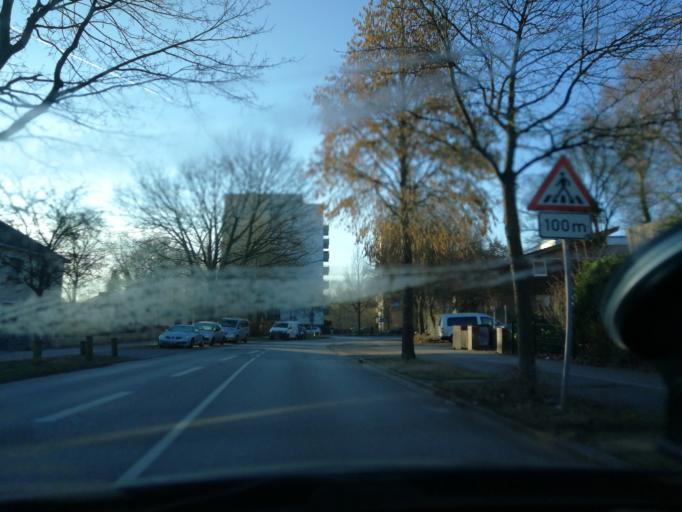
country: DE
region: Hamburg
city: Harburg
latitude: 53.4617
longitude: 9.9575
